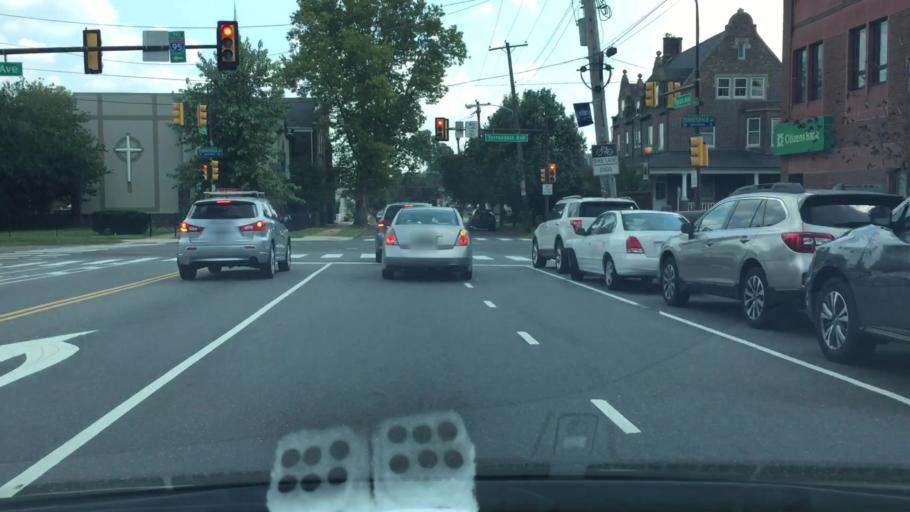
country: US
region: New Jersey
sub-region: Burlington County
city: Palmyra
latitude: 40.0274
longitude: -75.0413
